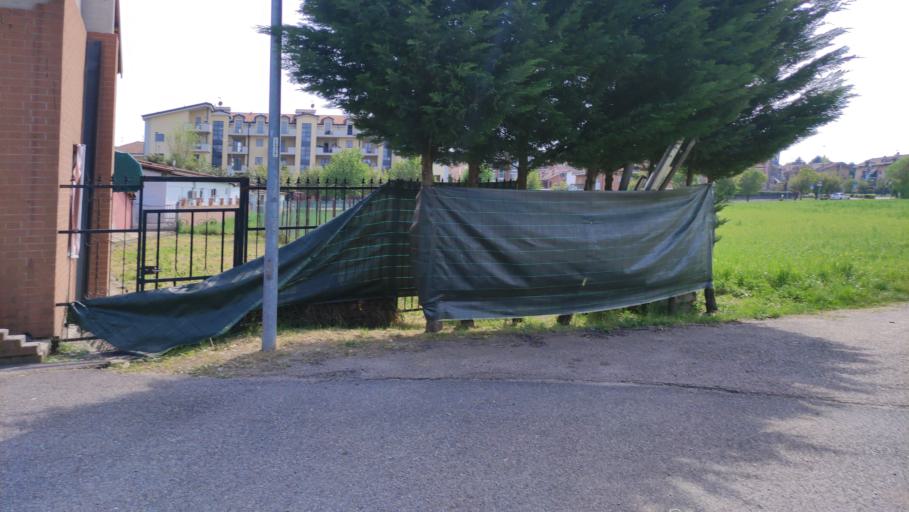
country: IT
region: Piedmont
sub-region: Provincia di Torino
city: Nichelino
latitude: 45.0055
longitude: 7.6437
